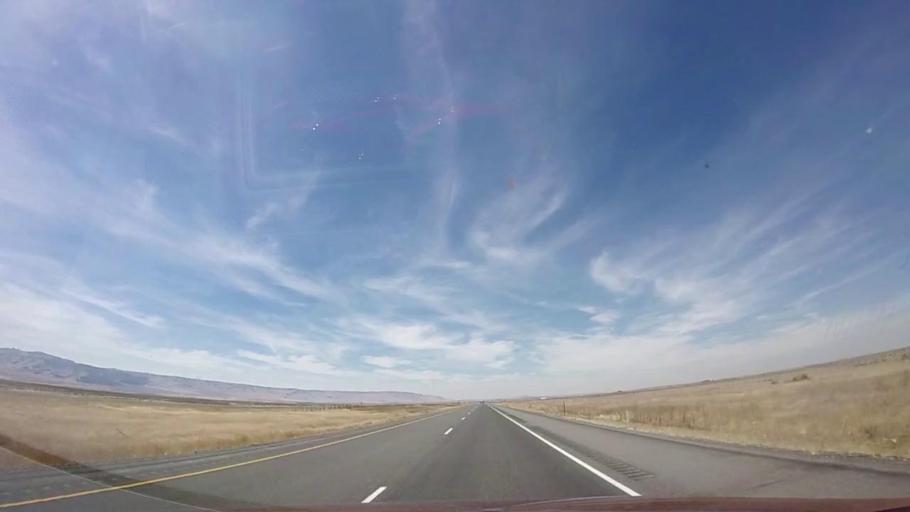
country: US
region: Idaho
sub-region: Minidoka County
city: Rupert
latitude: 42.3775
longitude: -113.2747
